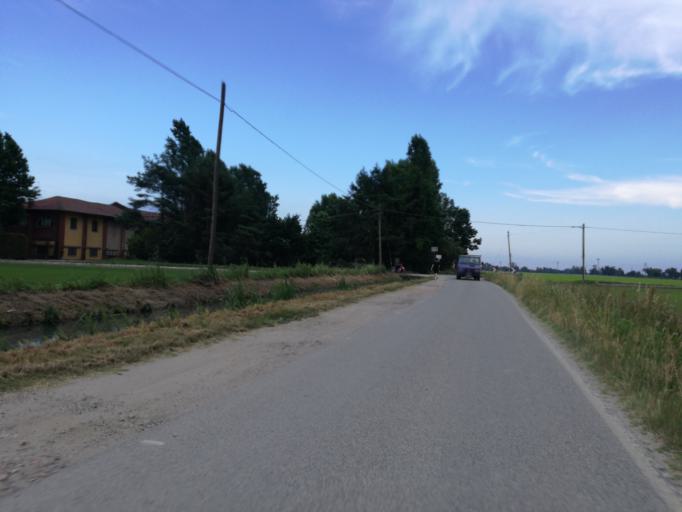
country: IT
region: Piedmont
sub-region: Provincia di Novara
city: Torrion Quartara
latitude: 45.4040
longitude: 8.6194
